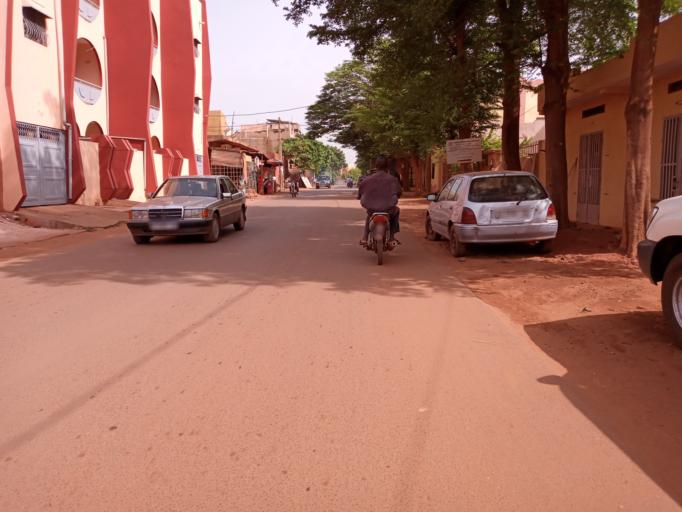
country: ML
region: Bamako
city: Bamako
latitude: 12.6055
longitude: -7.9508
